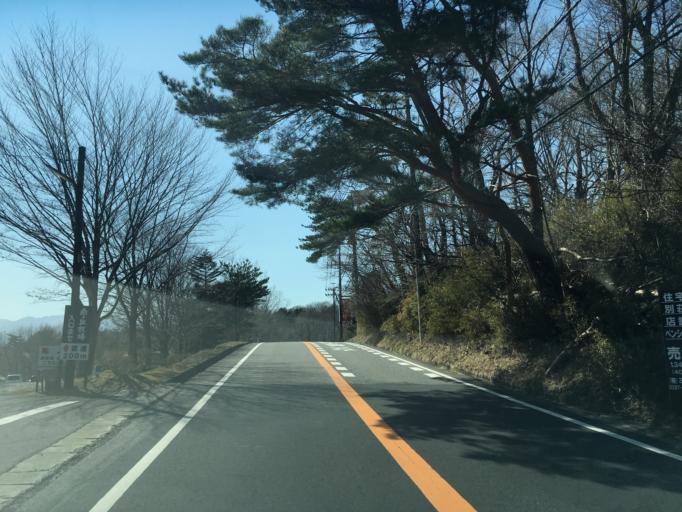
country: JP
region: Tochigi
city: Kuroiso
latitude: 37.0795
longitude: 140.0029
